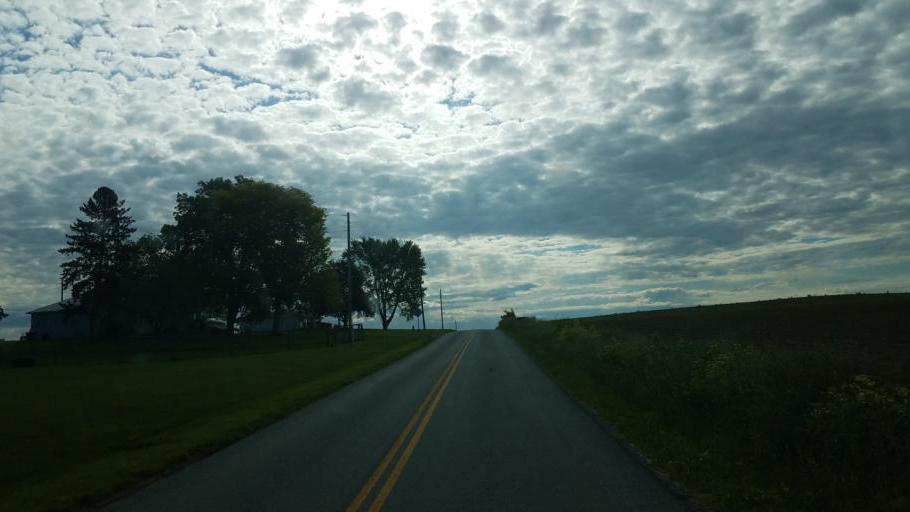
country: US
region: Ohio
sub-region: Medina County
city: Lodi
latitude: 40.9887
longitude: -81.9855
